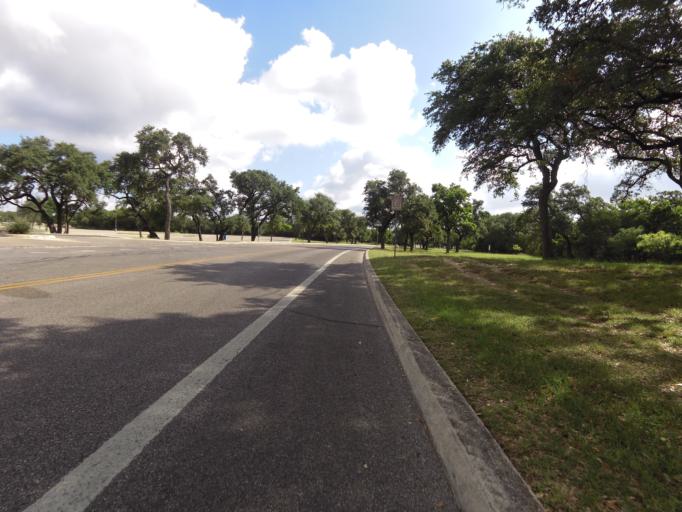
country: US
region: Texas
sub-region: Bexar County
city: Shavano Park
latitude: 29.5813
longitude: -98.6089
